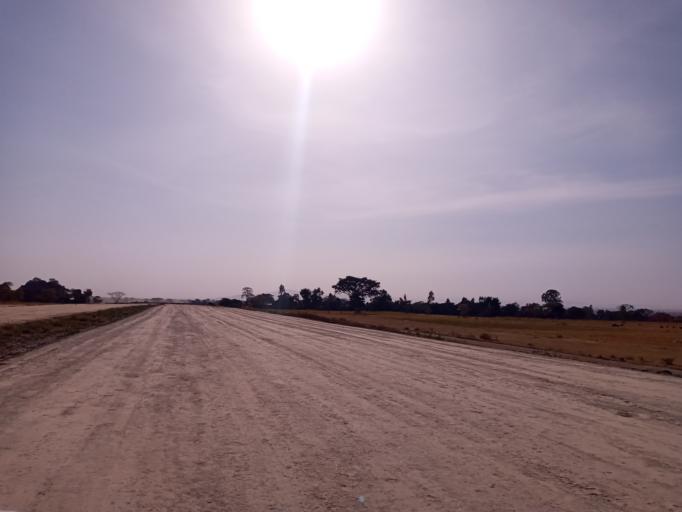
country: ET
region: Oromiya
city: Shashemene
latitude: 7.3120
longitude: 38.6247
